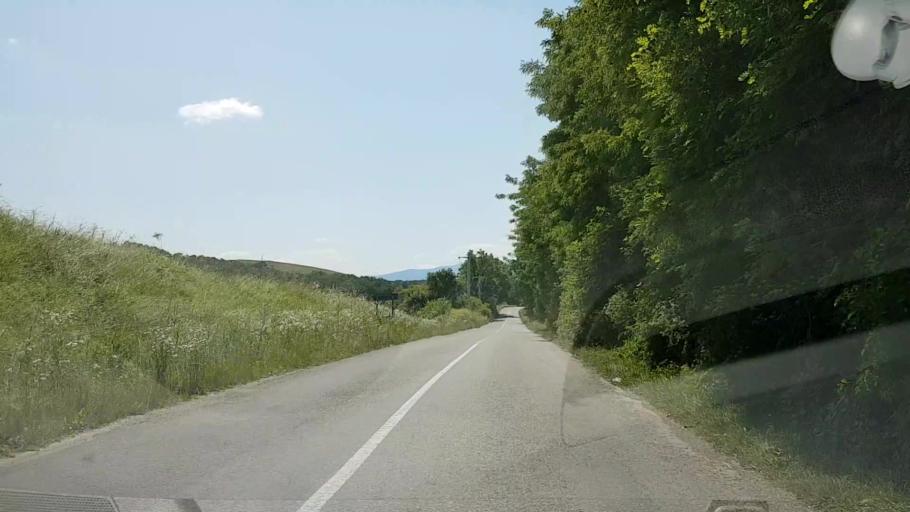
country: RO
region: Brasov
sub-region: Comuna Cincu
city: Cincu
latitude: 45.8688
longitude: 24.8230
